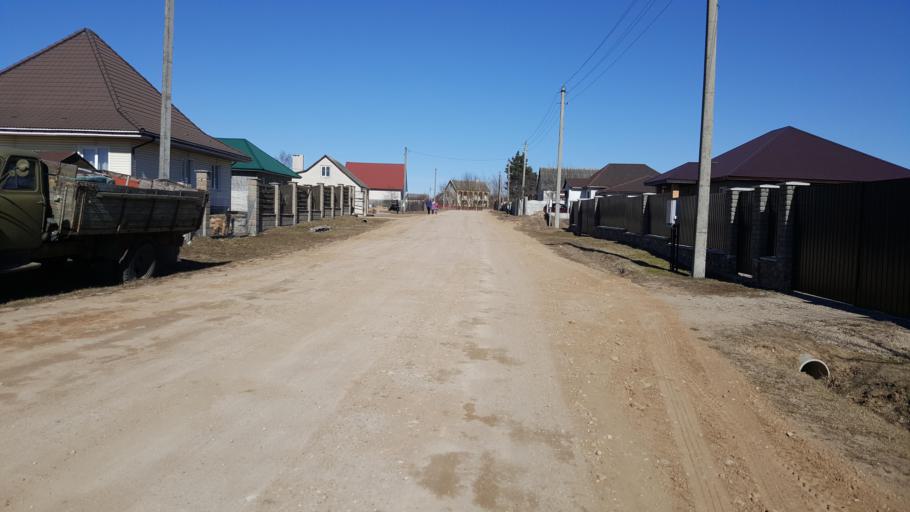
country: BY
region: Brest
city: Kamyanyets
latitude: 52.4012
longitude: 23.8441
